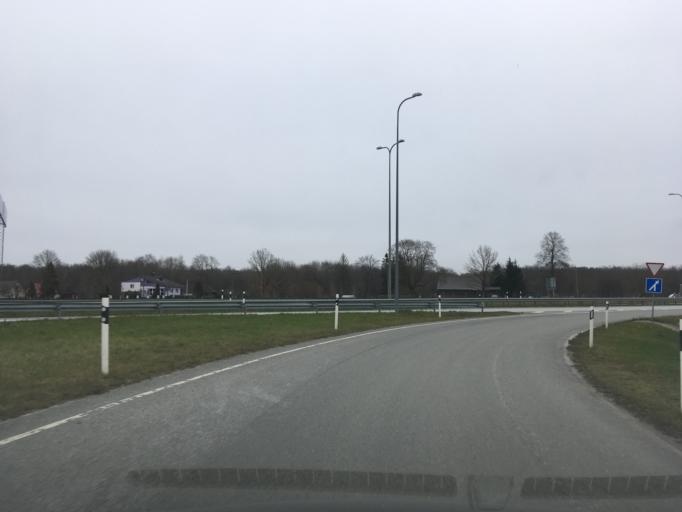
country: EE
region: Ida-Virumaa
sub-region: Johvi vald
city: Johvi
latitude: 59.3681
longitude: 27.3947
